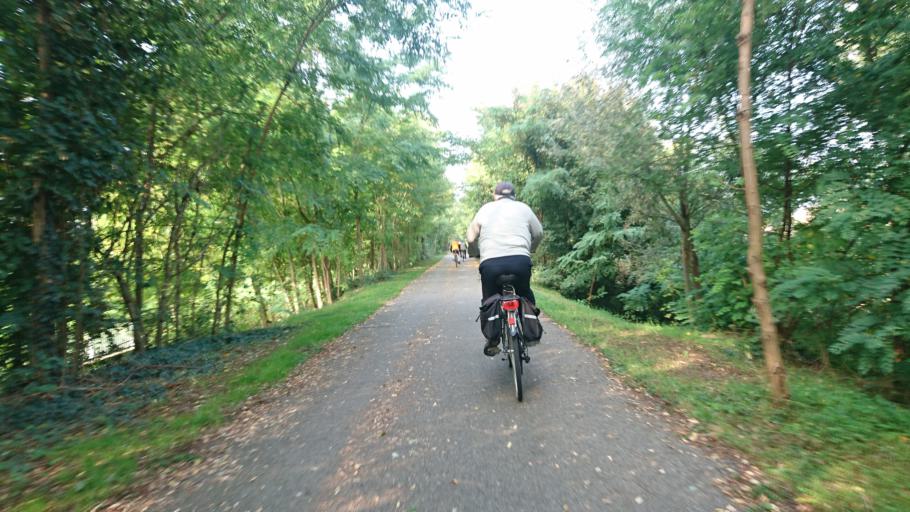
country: IT
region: Veneto
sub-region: Provincia di Padova
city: Pieve
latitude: 45.5383
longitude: 11.8184
